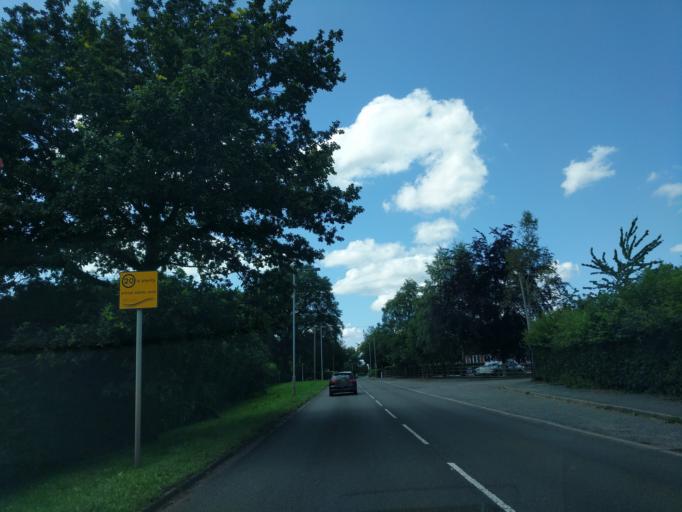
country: GB
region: England
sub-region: Staffordshire
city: Cheadle
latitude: 52.9386
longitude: -1.9567
